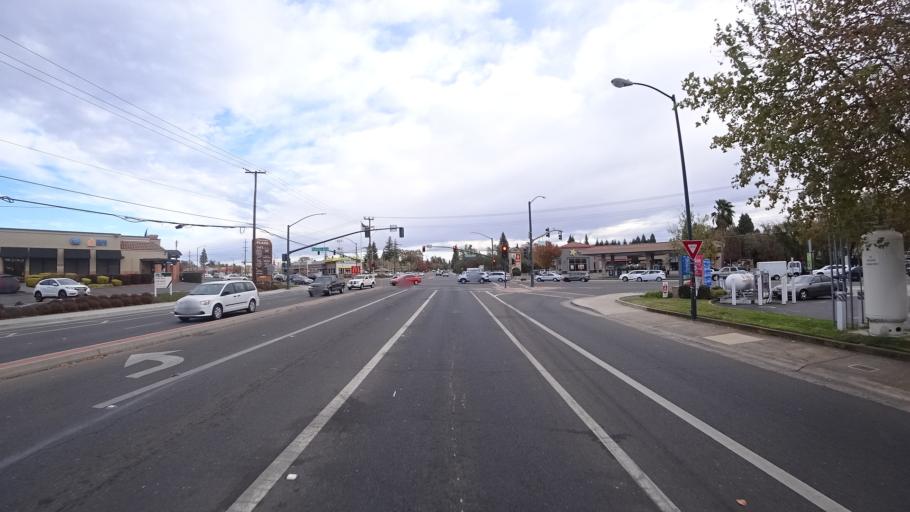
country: US
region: California
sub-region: Sacramento County
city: Citrus Heights
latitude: 38.7034
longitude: -121.2724
